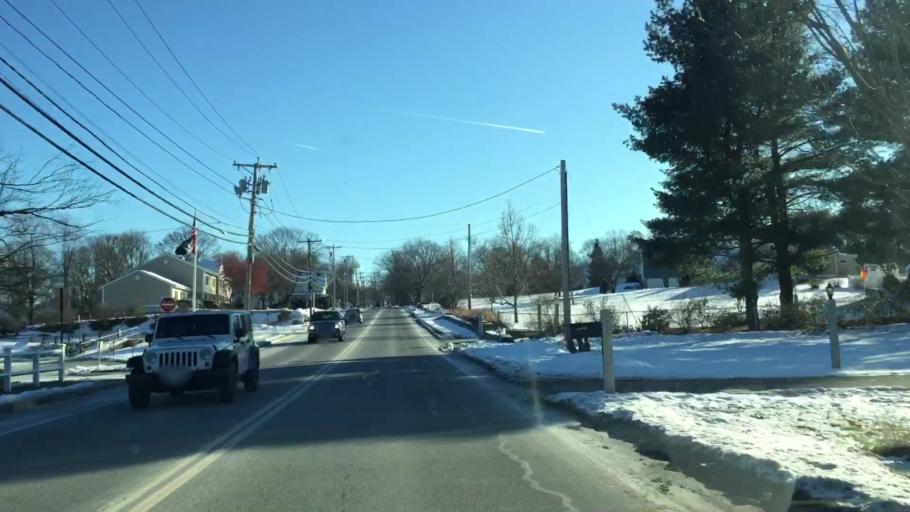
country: US
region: Massachusetts
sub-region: Middlesex County
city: Dracut
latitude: 42.6735
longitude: -71.3516
